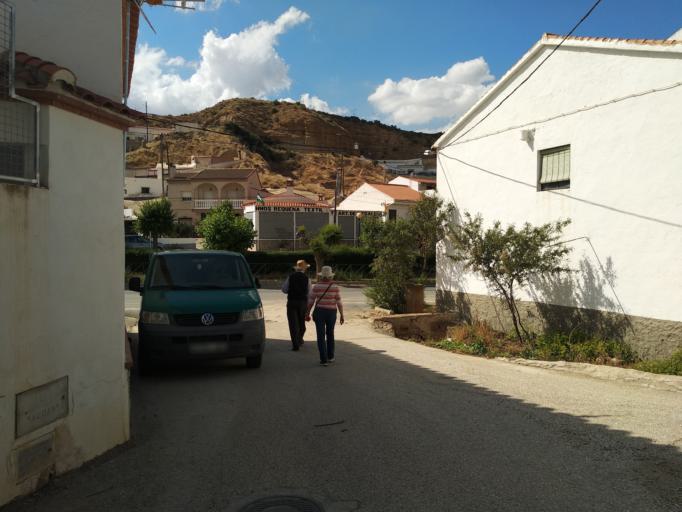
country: ES
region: Andalusia
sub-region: Provincia de Granada
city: Marchal
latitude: 37.3025
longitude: -3.2112
